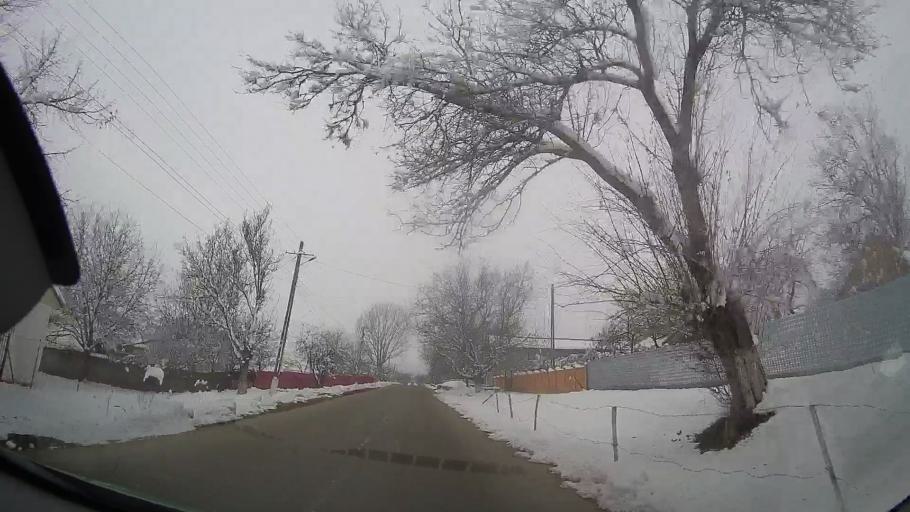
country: RO
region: Neamt
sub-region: Comuna Oniceni
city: Oniceni
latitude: 46.8126
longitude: 27.1949
